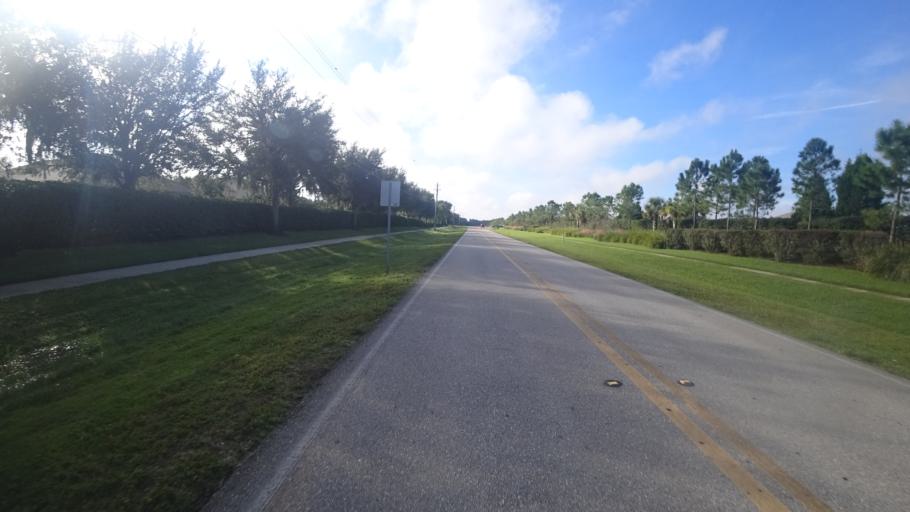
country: US
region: Florida
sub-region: Manatee County
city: Ellenton
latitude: 27.5552
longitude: -82.4459
